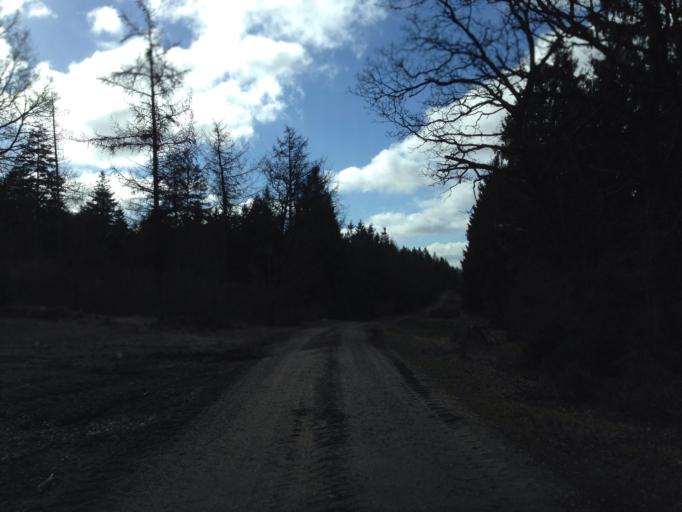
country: DK
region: Central Jutland
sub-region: Holstebro Kommune
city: Ulfborg
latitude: 56.2739
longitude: 8.4638
